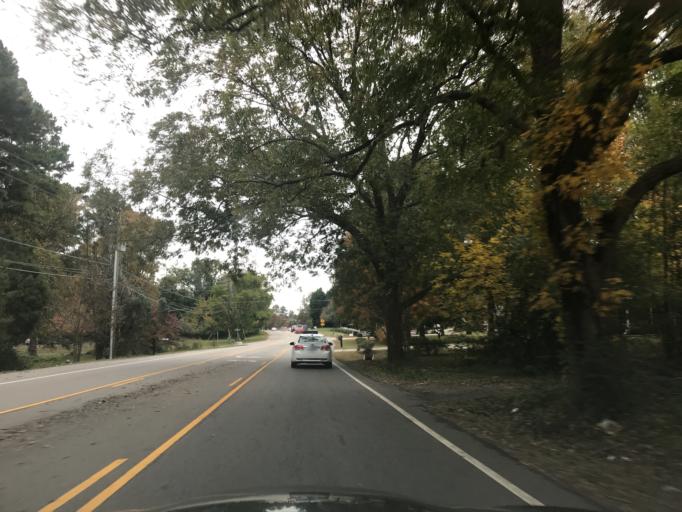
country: US
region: North Carolina
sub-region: Wake County
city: Raleigh
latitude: 35.8659
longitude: -78.5980
